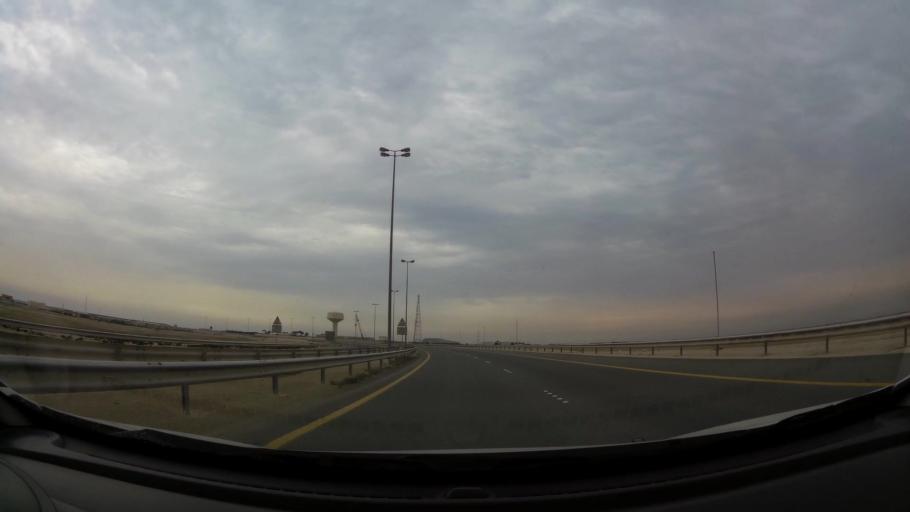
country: BH
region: Central Governorate
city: Dar Kulayb
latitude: 25.8440
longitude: 50.5845
